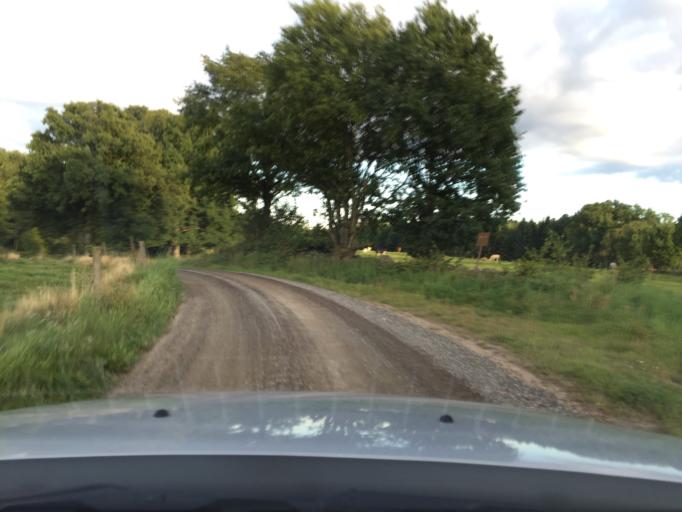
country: SE
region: Skane
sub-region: Hassleholms Kommun
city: Sosdala
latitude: 56.0298
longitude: 13.7203
